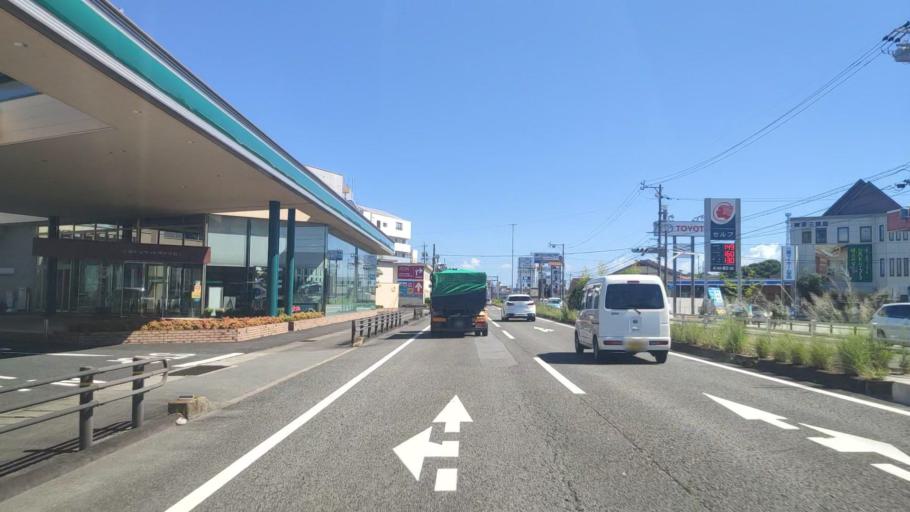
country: JP
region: Mie
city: Tsu-shi
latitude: 34.7004
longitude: 136.5079
